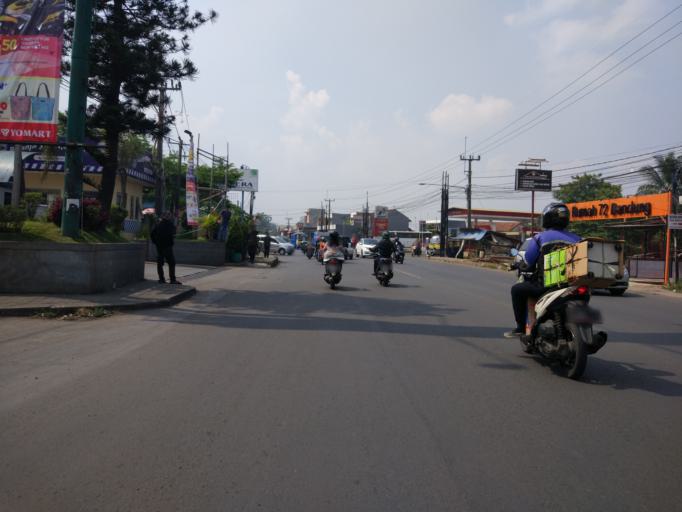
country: ID
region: West Java
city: Cileunyi
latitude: -6.9383
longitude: 107.7338
